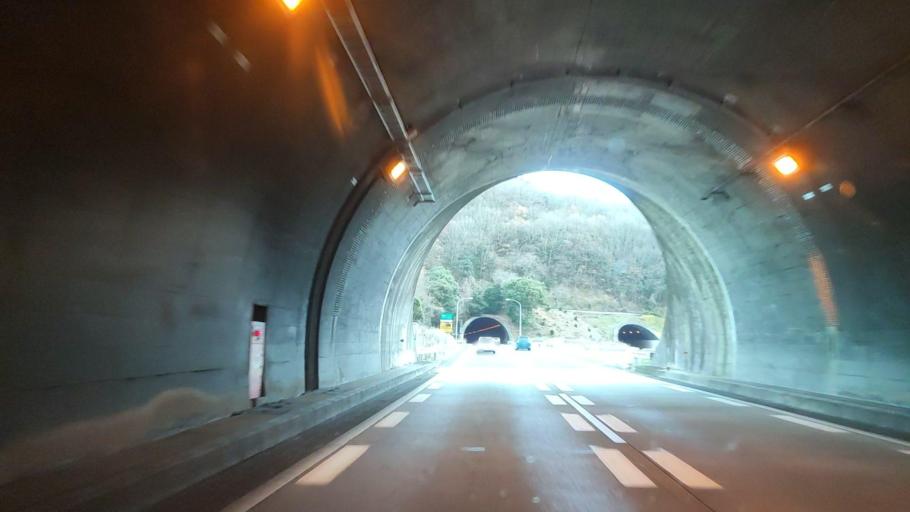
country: JP
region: Hiroshima
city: Fukuyama
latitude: 34.5129
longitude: 133.3516
